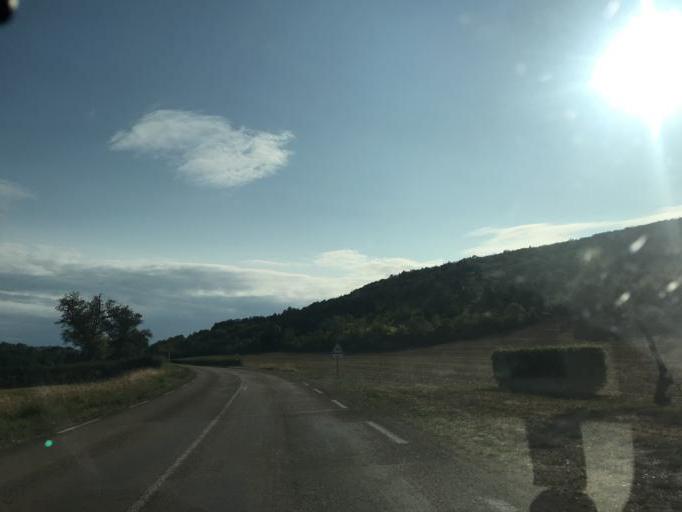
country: FR
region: Bourgogne
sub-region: Departement de l'Yonne
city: Joux-la-Ville
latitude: 47.5253
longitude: 3.7787
